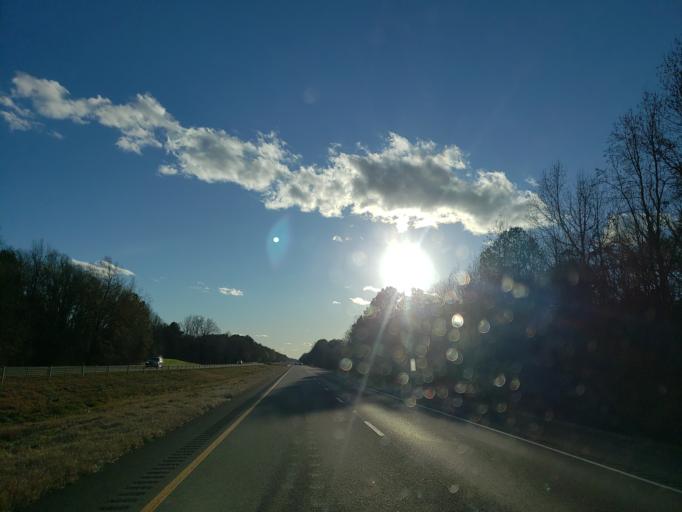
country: US
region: Alabama
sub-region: Greene County
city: Eutaw
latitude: 32.7820
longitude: -88.0497
